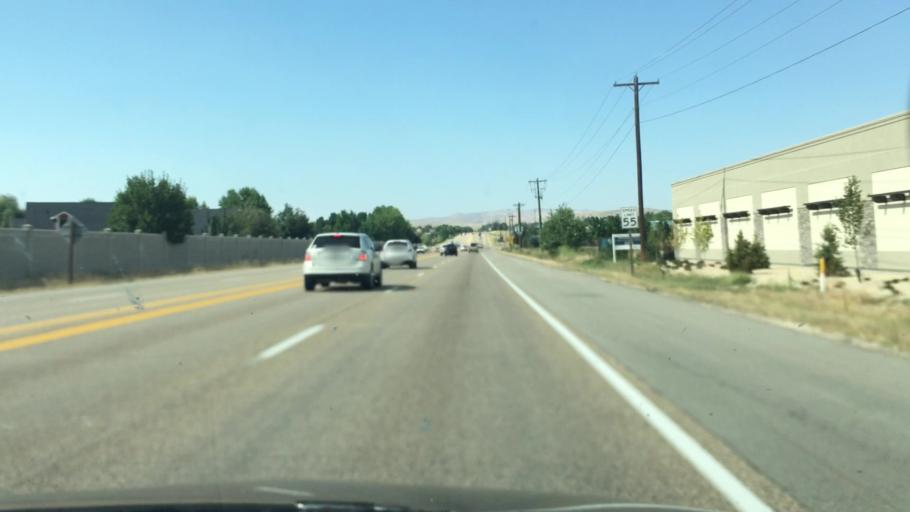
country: US
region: Idaho
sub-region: Ada County
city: Eagle
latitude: 43.6896
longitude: -116.3192
